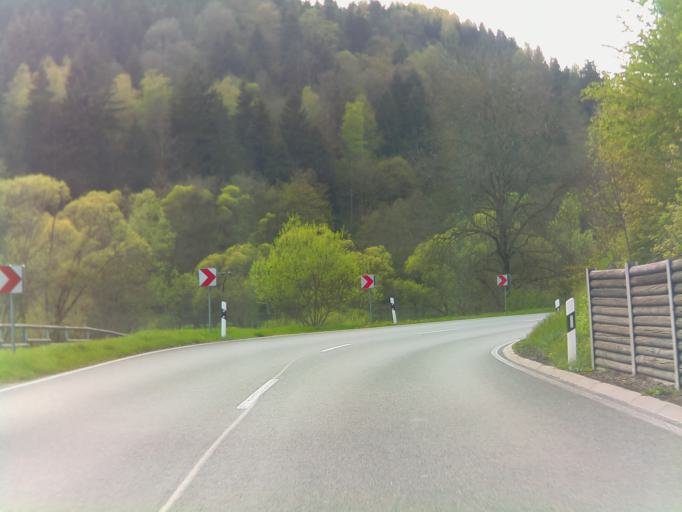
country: DE
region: Thuringia
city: Probstzella
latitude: 50.5412
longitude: 11.3711
